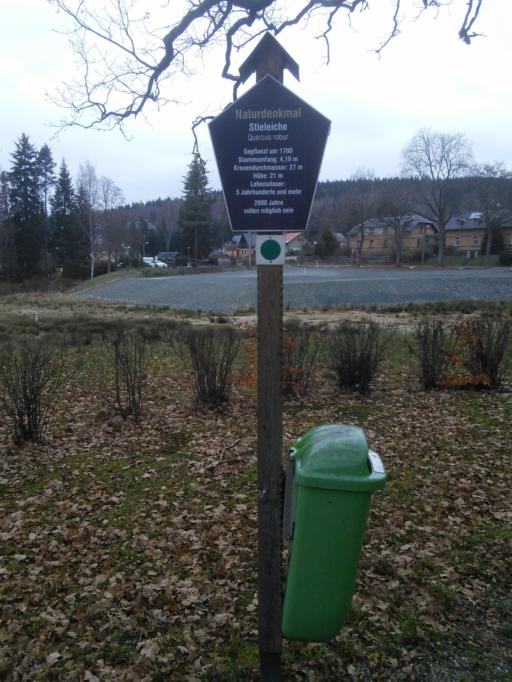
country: DE
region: Saxony
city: Bad Elster
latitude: 50.2736
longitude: 12.2485
